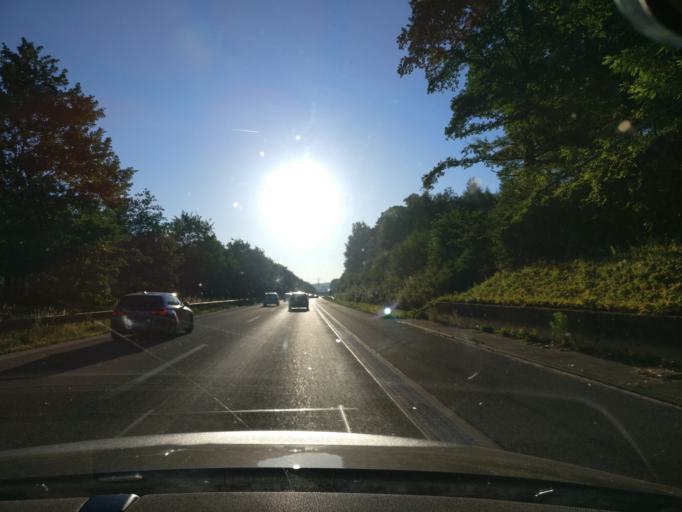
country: DE
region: North Rhine-Westphalia
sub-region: Regierungsbezirk Dusseldorf
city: Ratingen
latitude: 51.2760
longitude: 6.8425
